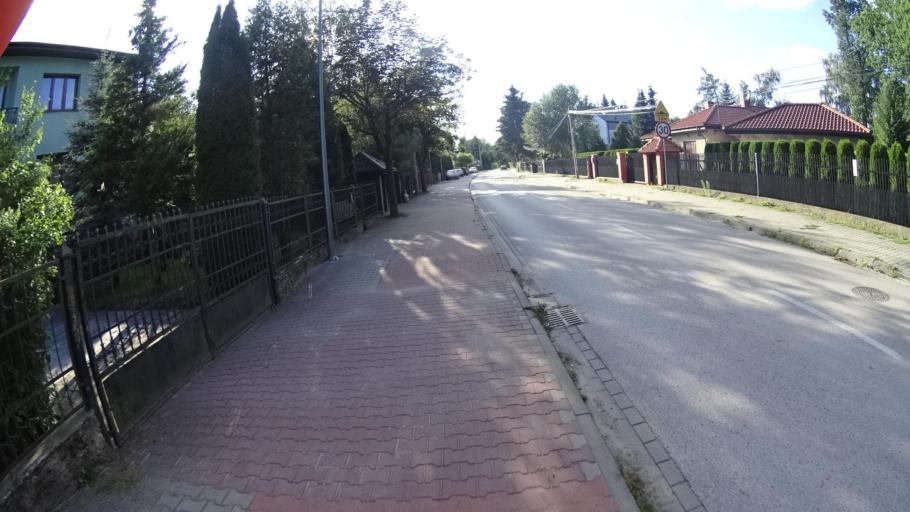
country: PL
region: Masovian Voivodeship
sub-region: Powiat piaseczynski
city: Piaseczno
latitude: 52.0653
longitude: 20.9949
